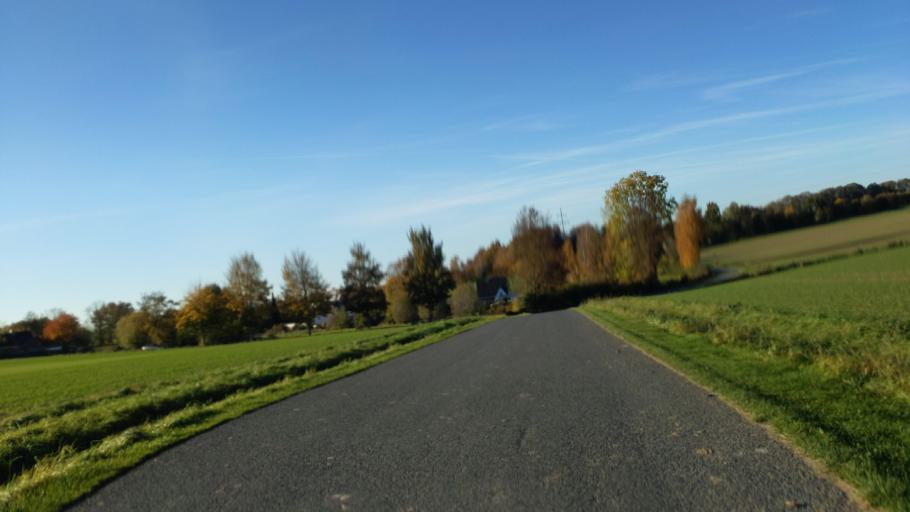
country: DE
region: Schleswig-Holstein
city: Gross Disnack
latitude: 53.7434
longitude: 10.6973
